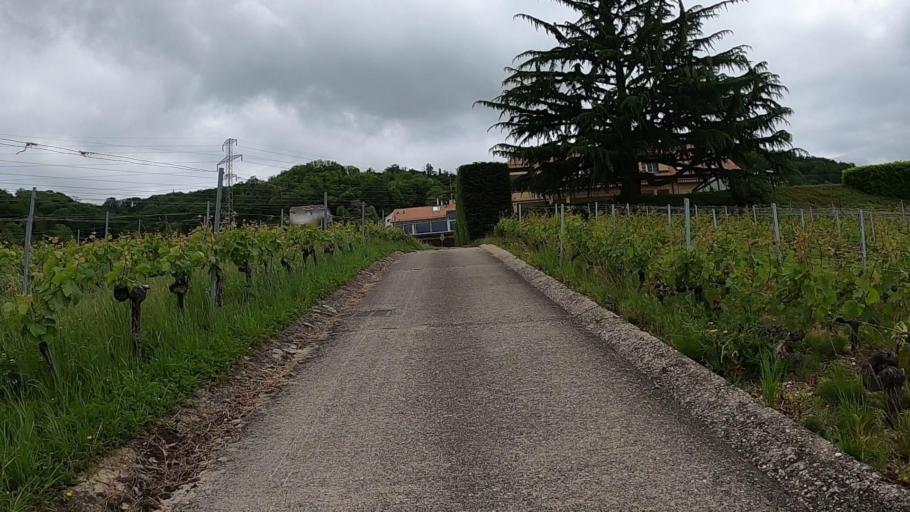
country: CH
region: Vaud
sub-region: Nyon District
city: Rolle
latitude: 46.4742
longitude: 6.3337
